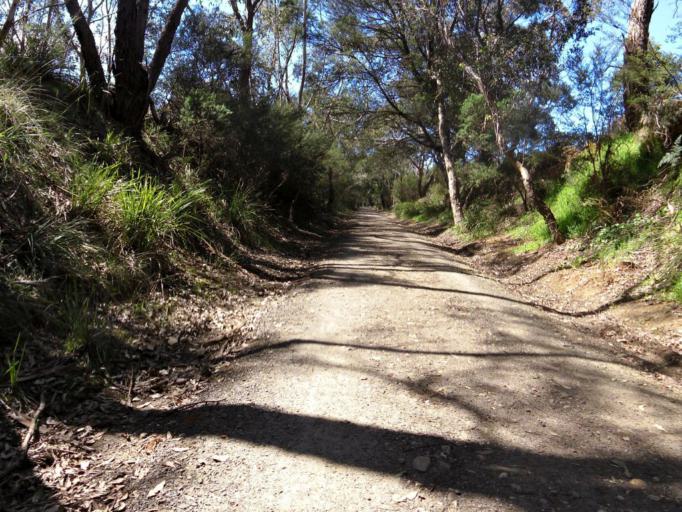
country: AU
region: Victoria
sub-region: Latrobe
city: Moe
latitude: -38.1744
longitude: 146.2779
